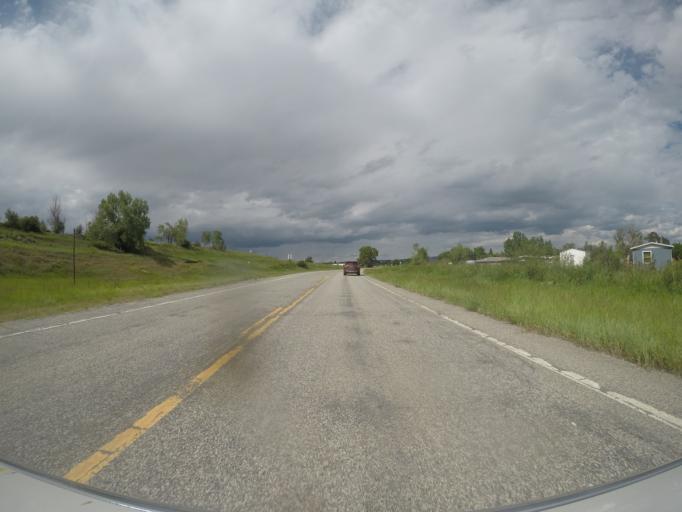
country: US
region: Montana
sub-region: Sweet Grass County
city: Big Timber
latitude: 45.8228
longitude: -109.9531
